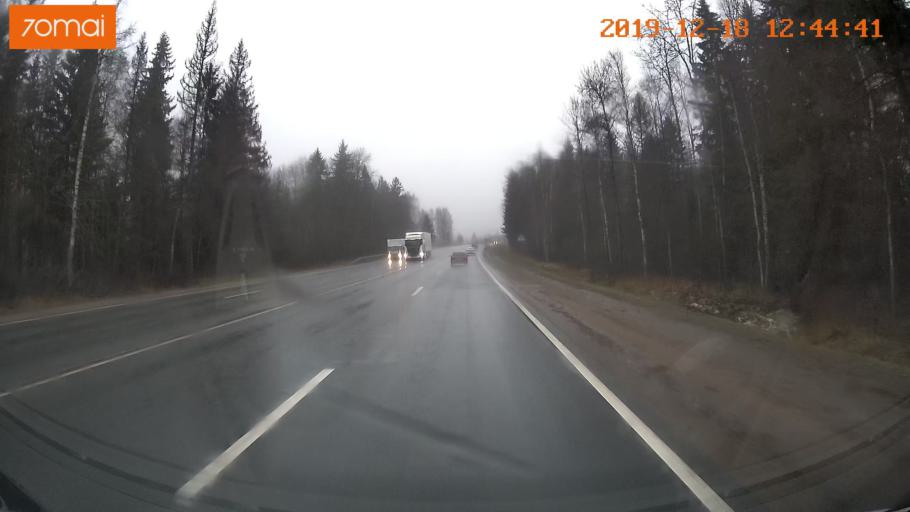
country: RU
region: Moskovskaya
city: Vysokovsk
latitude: 56.2224
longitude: 36.6502
